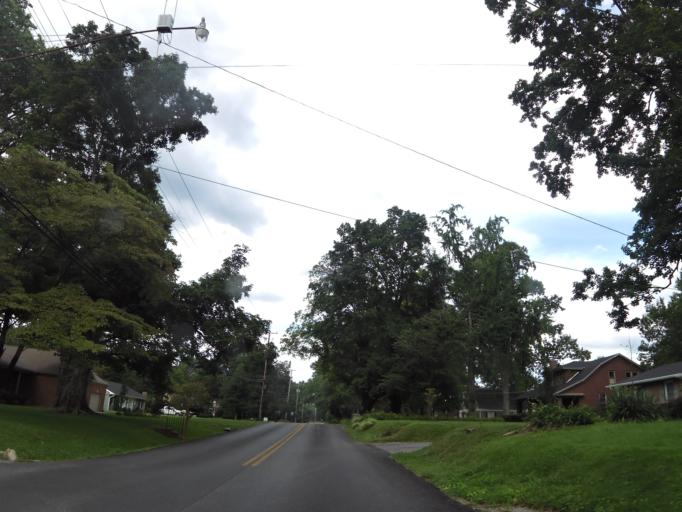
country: US
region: Kentucky
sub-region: Christian County
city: Hopkinsville
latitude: 36.8517
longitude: -87.5061
